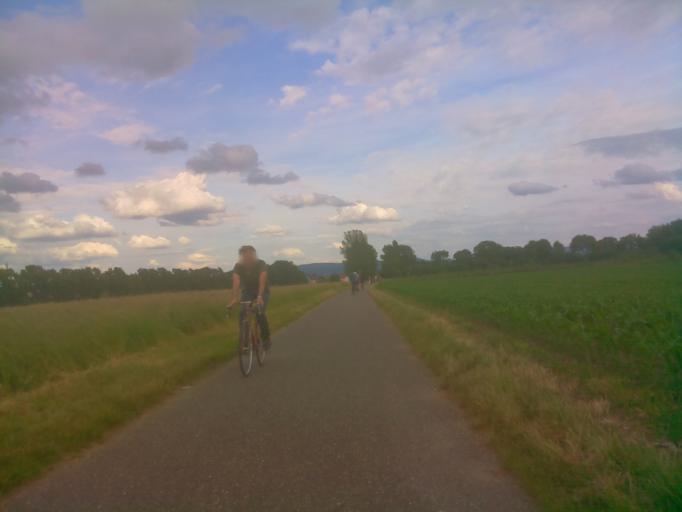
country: DE
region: Baden-Wuerttemberg
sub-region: Karlsruhe Region
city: Ilvesheim
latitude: 49.4757
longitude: 8.5511
